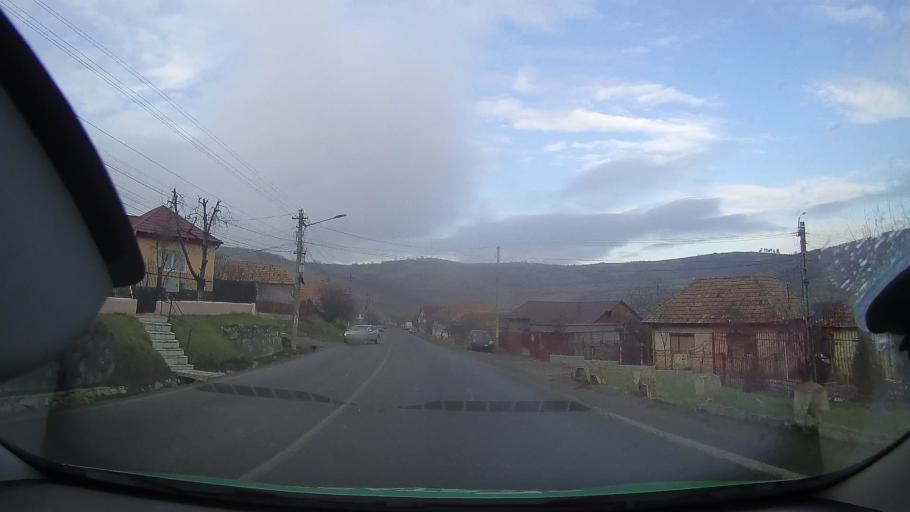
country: RO
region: Mures
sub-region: Municipiul Tarnaveni
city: Tarnaveni
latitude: 46.3366
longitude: 24.2839
